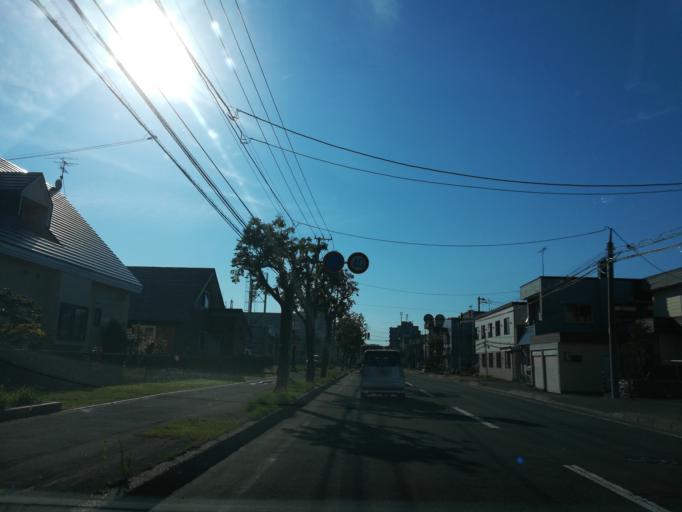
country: JP
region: Hokkaido
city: Sapporo
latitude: 43.0198
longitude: 141.4496
